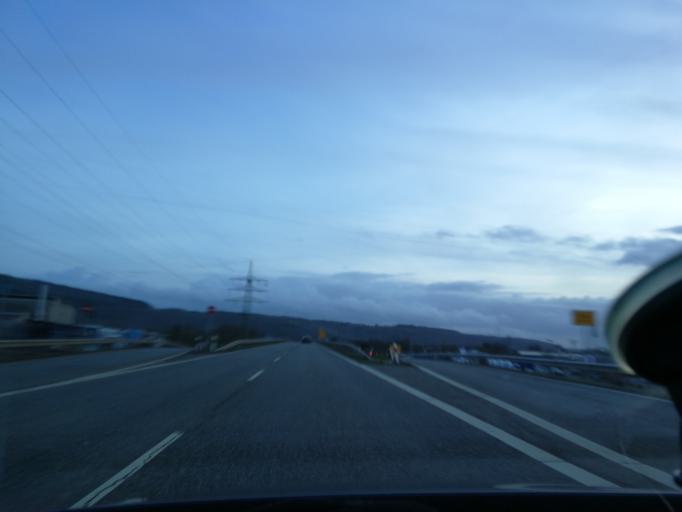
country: DE
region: Rheinland-Pfalz
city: Kenn
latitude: 49.7939
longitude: 6.6891
